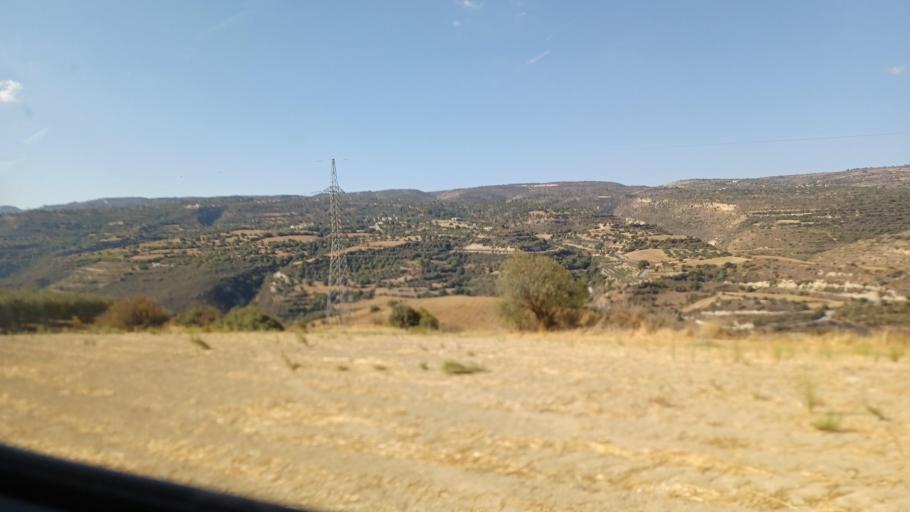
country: CY
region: Pafos
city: Polis
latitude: 34.9675
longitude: 32.4645
